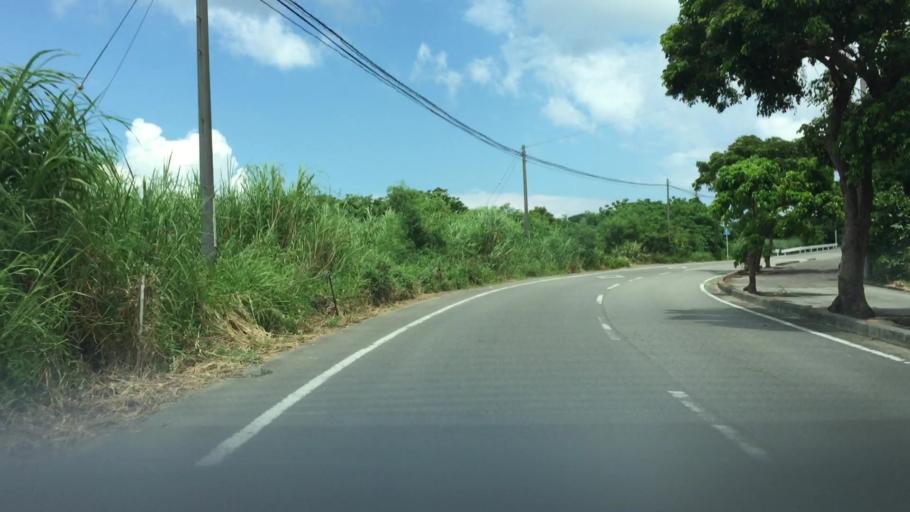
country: JP
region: Okinawa
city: Ishigaki
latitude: 24.3650
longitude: 124.1401
